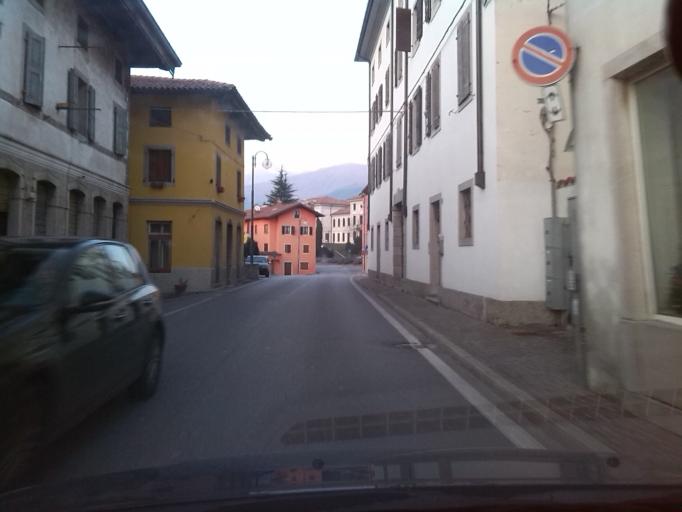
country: IT
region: Friuli Venezia Giulia
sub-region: Provincia di Udine
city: San Pietro al Natisone
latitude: 46.1286
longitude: 13.4859
